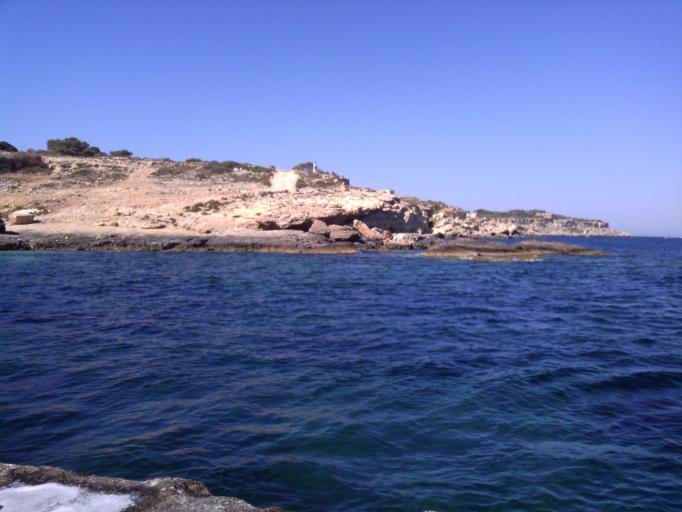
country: MT
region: Il-Mellieha
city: Mellieha
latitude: 35.9799
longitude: 14.3612
